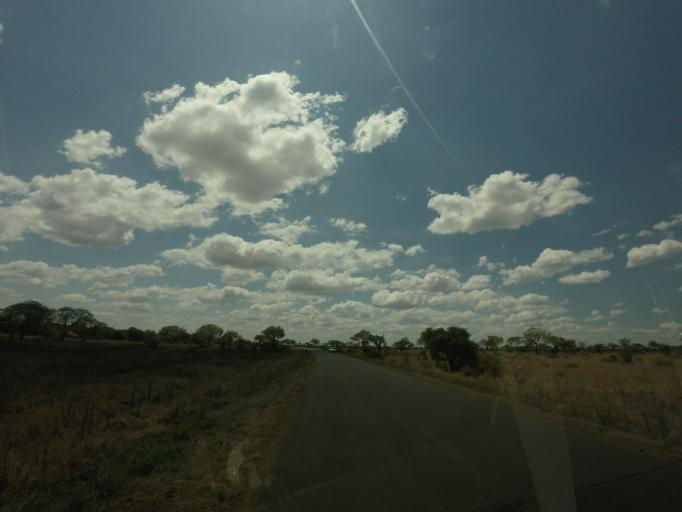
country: ZA
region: Limpopo
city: Thulamahashi
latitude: -24.3929
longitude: 31.7831
